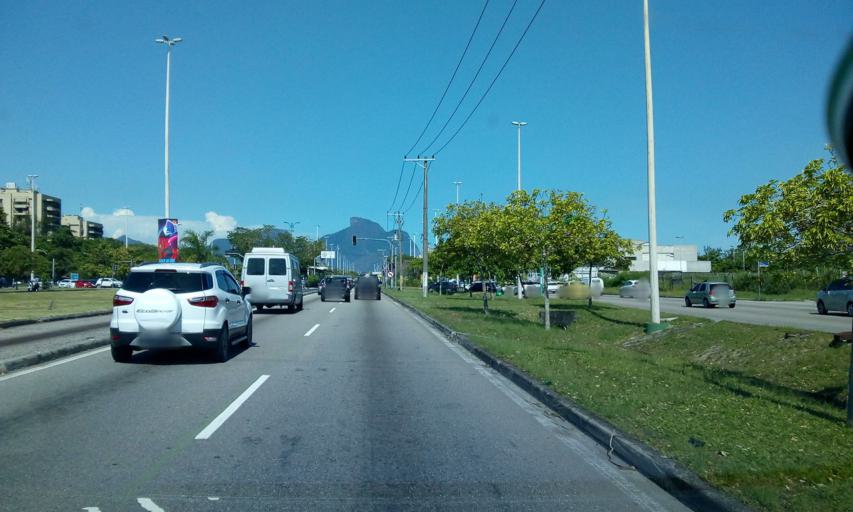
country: BR
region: Rio de Janeiro
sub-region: Nilopolis
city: Nilopolis
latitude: -23.0005
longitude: -43.3794
